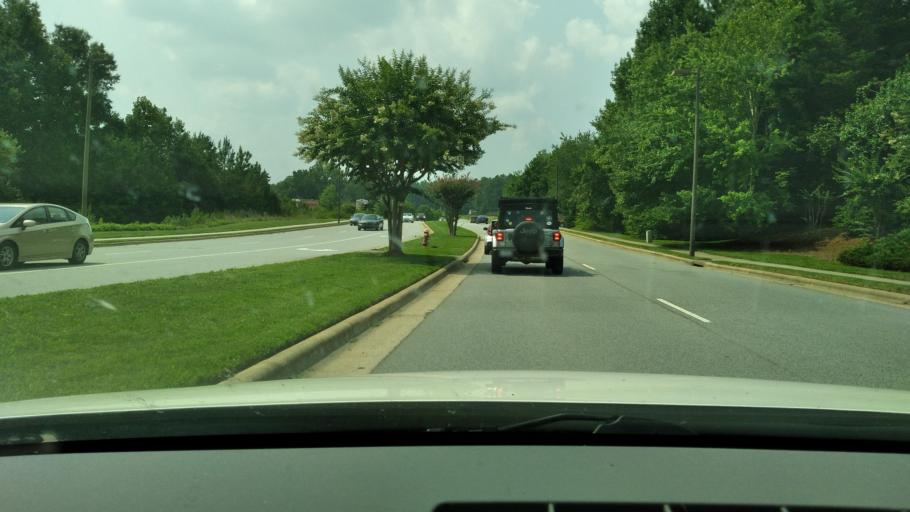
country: US
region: North Carolina
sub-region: Guilford County
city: Jamestown
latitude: 36.0428
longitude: -79.9245
